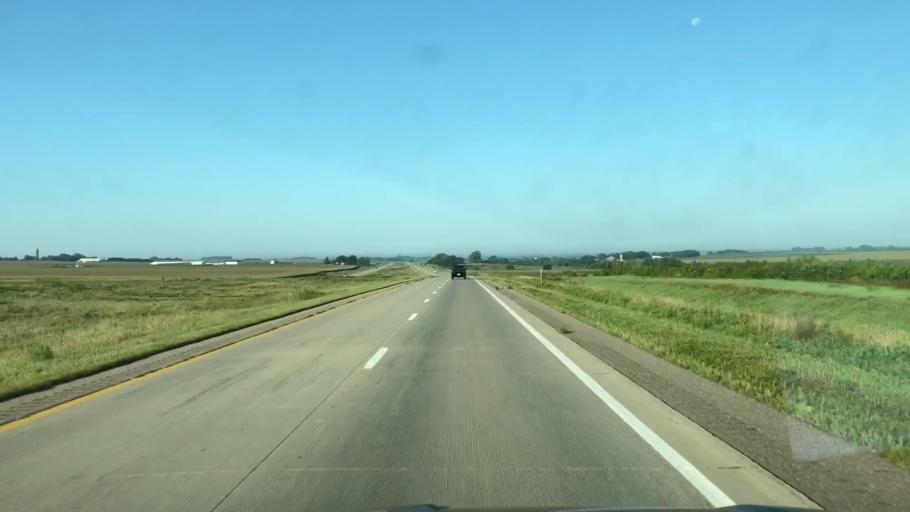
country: US
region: Iowa
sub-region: Sioux County
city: Alton
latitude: 43.0331
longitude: -95.9276
